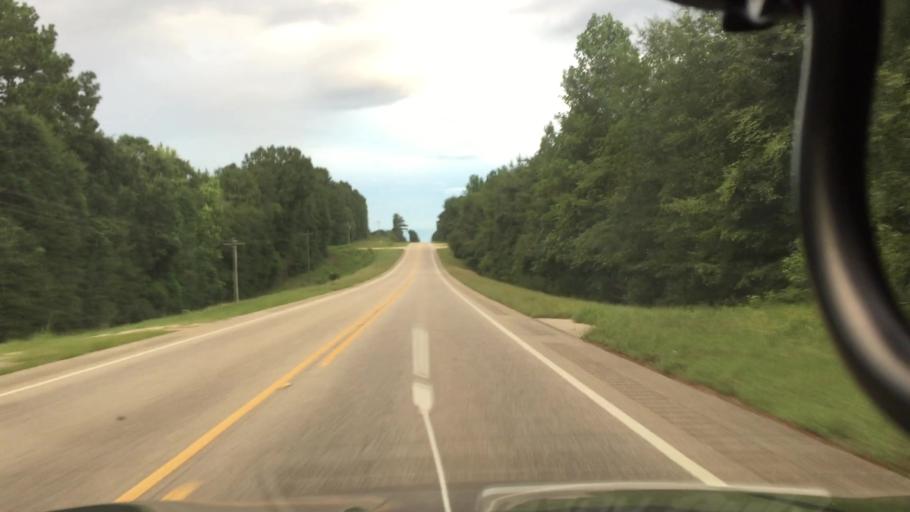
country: US
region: Alabama
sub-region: Pike County
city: Brundidge
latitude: 31.6585
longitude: -85.9520
